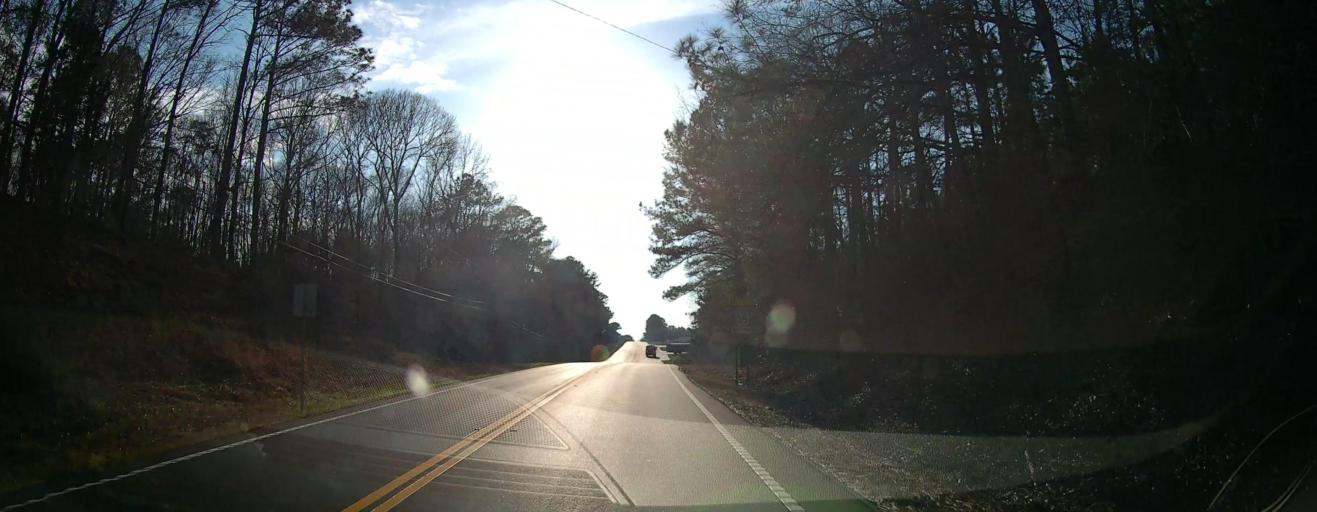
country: US
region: Georgia
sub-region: Harris County
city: Hamilton
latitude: 32.7574
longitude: -84.8846
